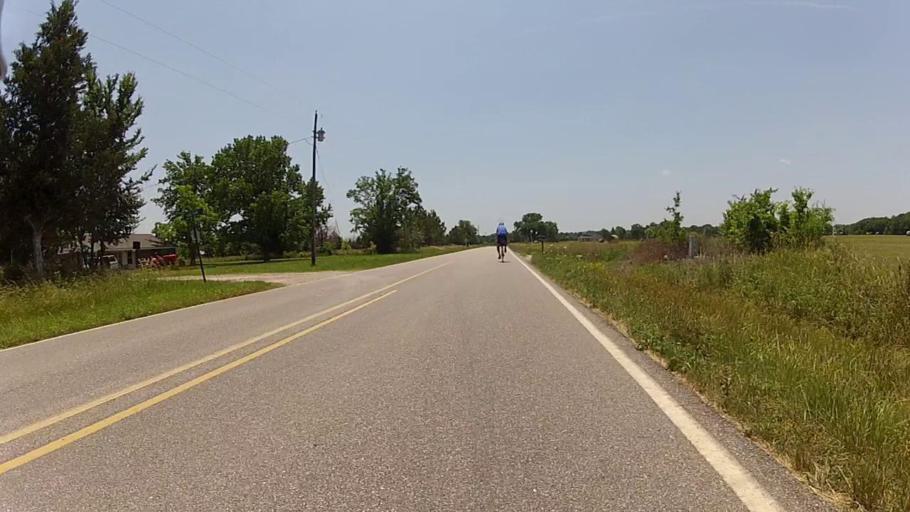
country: US
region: Kansas
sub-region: Montgomery County
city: Cherryvale
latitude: 37.2214
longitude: -95.5382
